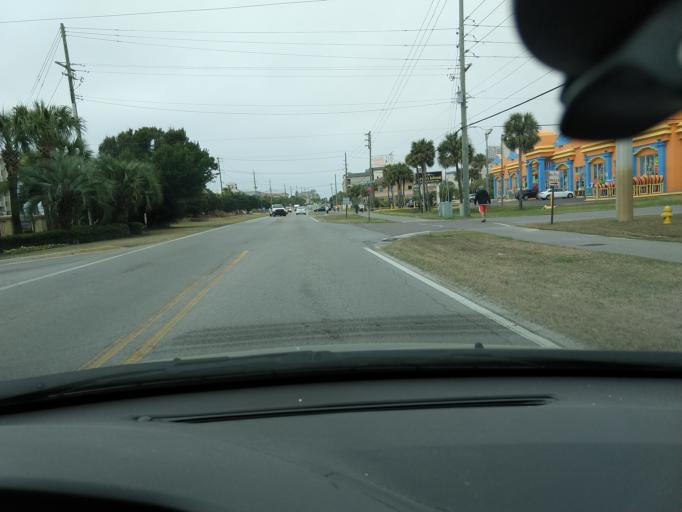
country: US
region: Florida
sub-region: Walton County
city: Miramar Beach
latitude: 30.3753
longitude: -86.3584
